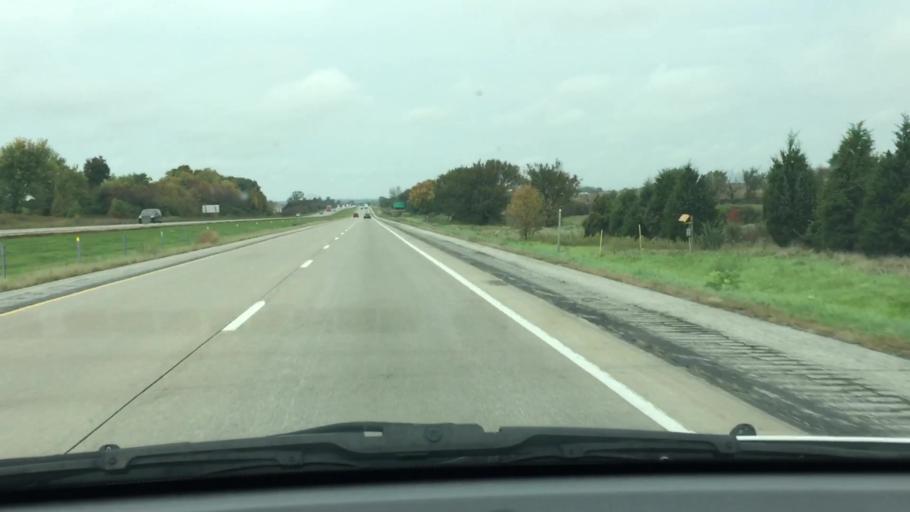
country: US
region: Iowa
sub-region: Johnson County
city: Iowa City
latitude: 41.6772
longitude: -91.4604
